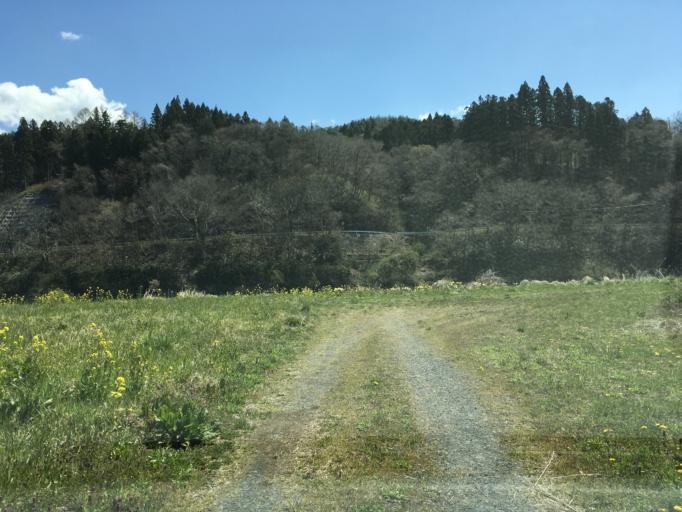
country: JP
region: Iwate
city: Ichinoseki
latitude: 38.8307
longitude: 141.2583
